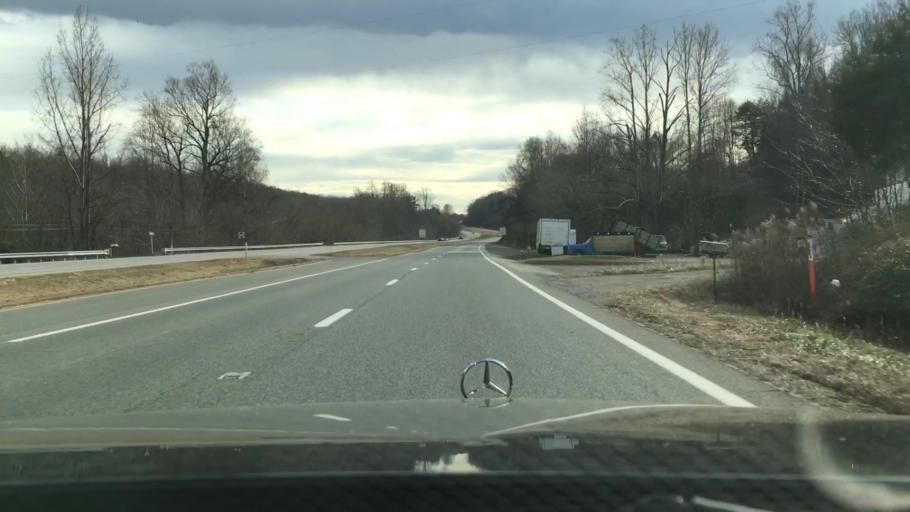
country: US
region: Virginia
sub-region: Pittsylvania County
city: Motley
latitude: 37.0213
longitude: -79.3578
